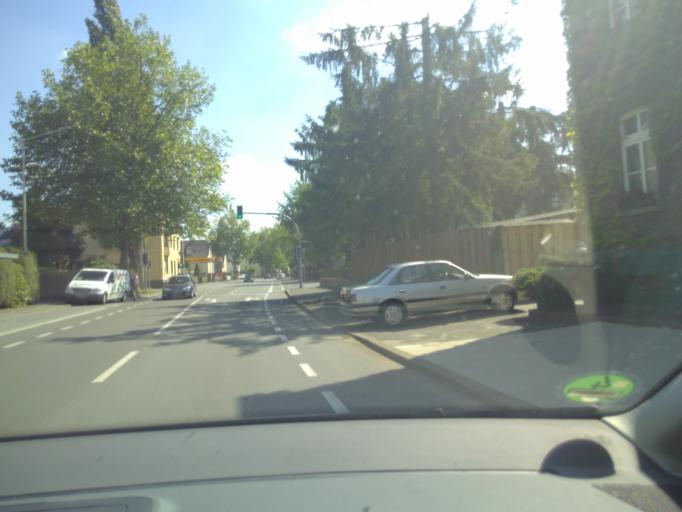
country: DE
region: North Rhine-Westphalia
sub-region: Regierungsbezirk Dusseldorf
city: Hilden
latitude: 51.1811
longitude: 6.9397
